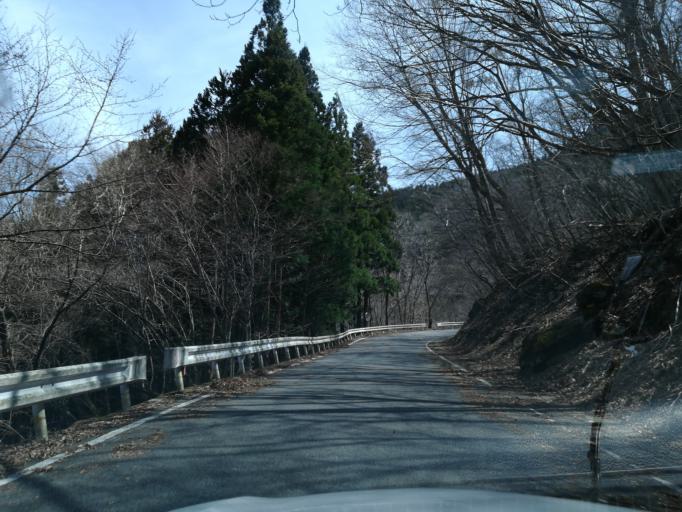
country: JP
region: Tokushima
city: Wakimachi
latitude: 33.8830
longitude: 134.0521
